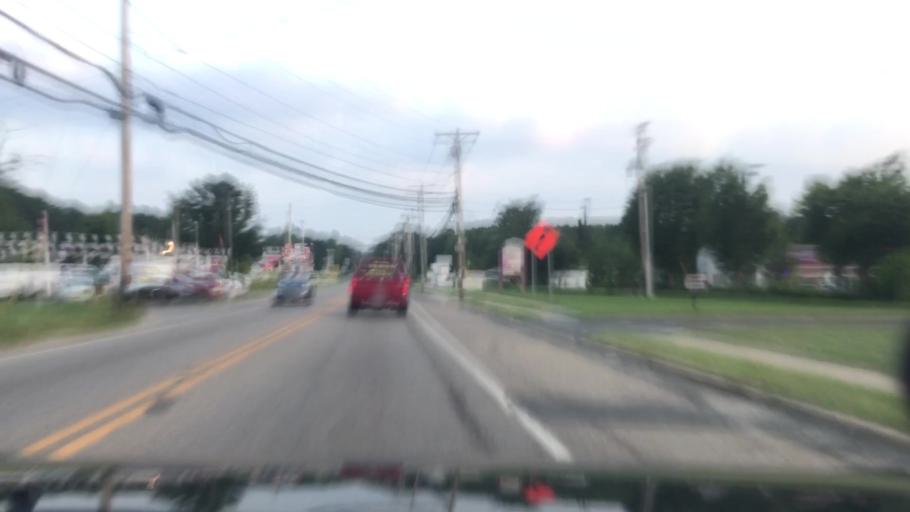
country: US
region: New Jersey
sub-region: Ocean County
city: Pine Lake Park
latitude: 40.0076
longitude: -74.2154
